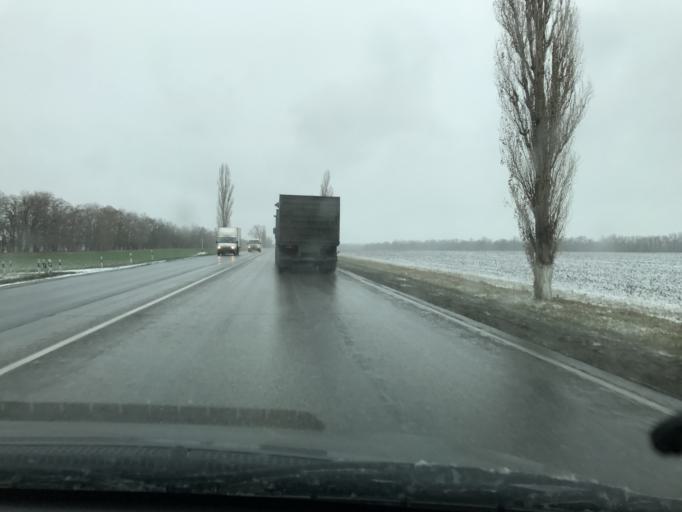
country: RU
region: Rostov
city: Kagal'nitskaya
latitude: 46.8410
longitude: 40.2211
